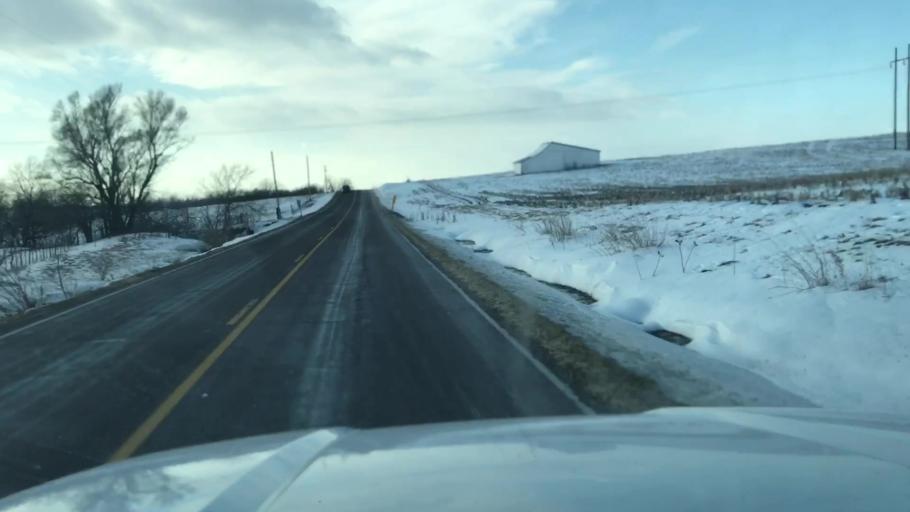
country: US
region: Missouri
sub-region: Nodaway County
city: Maryville
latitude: 40.2016
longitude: -94.9300
